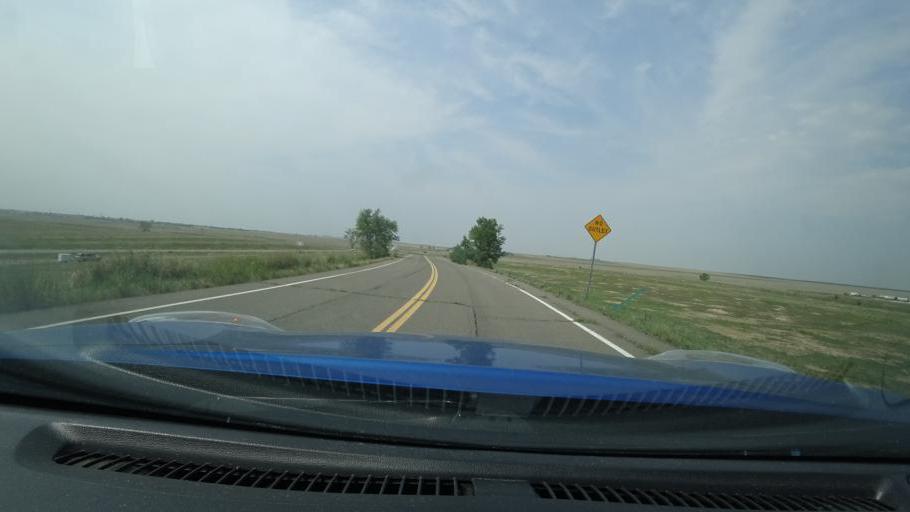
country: US
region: Colorado
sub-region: Adams County
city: Aurora
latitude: 39.7553
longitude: -104.7154
